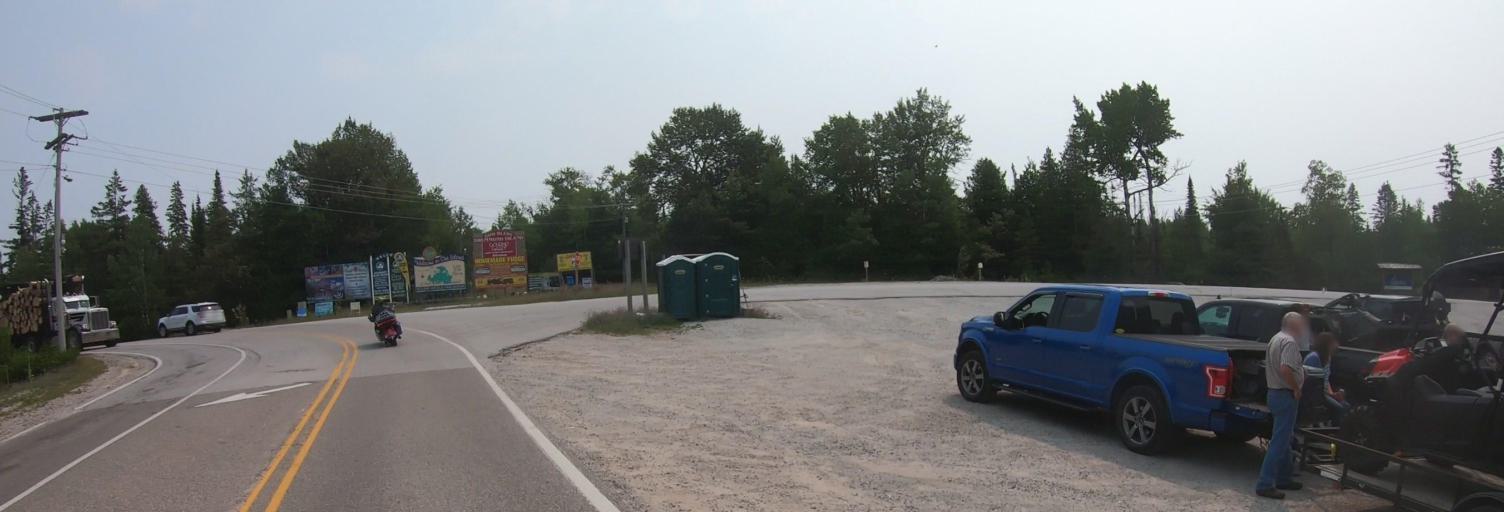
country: CA
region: Ontario
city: Thessalon
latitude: 45.9887
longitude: -83.8775
